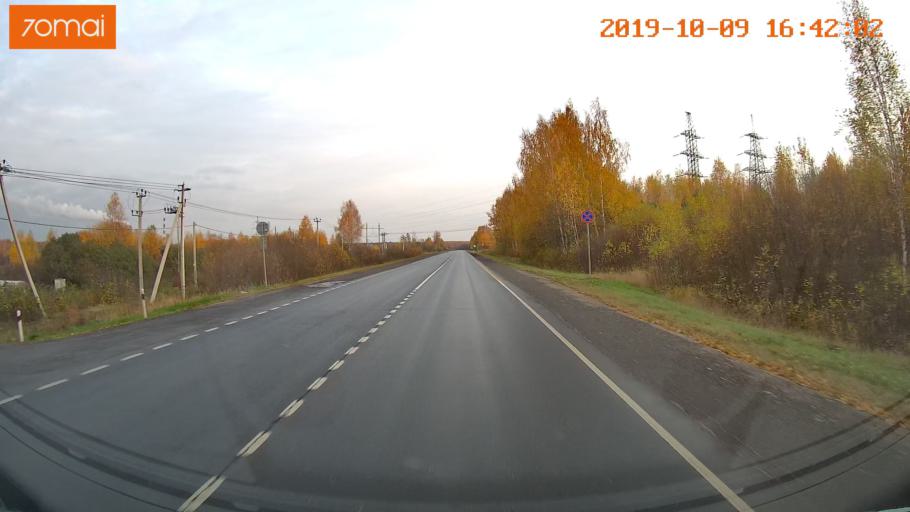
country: RU
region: Kostroma
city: Volgorechensk
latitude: 57.4666
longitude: 41.0924
